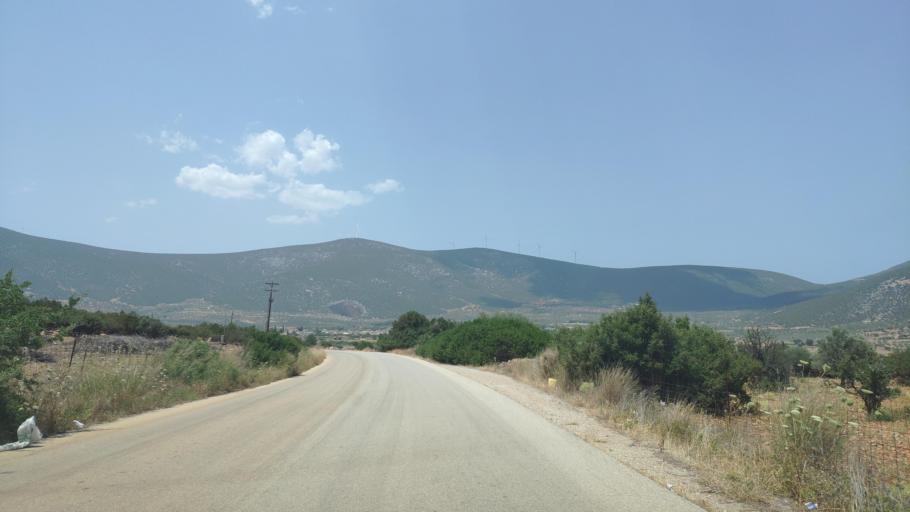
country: GR
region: Peloponnese
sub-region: Nomos Argolidos
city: Didyma
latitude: 37.4480
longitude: 23.1806
